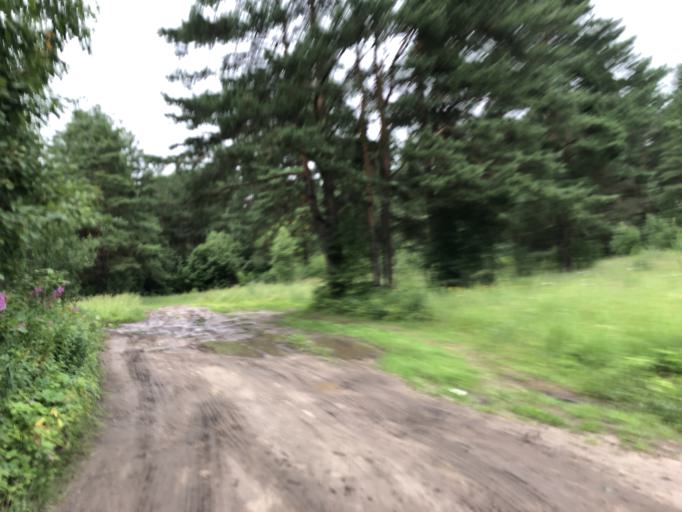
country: RU
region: Tverskaya
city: Rzhev
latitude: 56.2460
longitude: 34.3707
